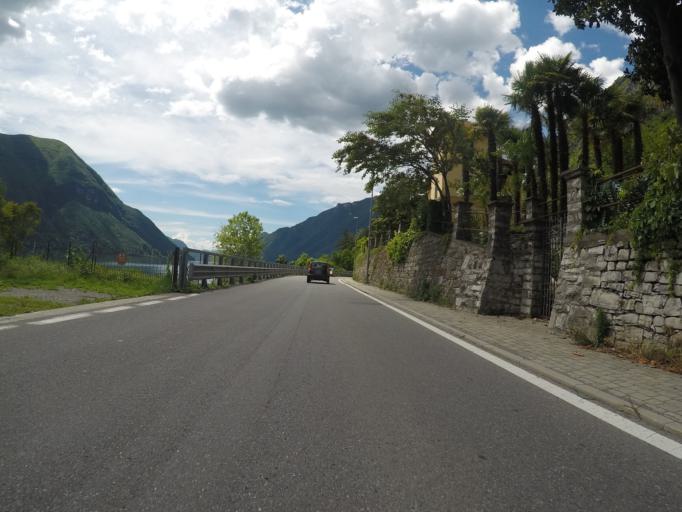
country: IT
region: Lombardy
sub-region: Provincia di Como
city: Osteno
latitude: 46.0242
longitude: 9.0875
